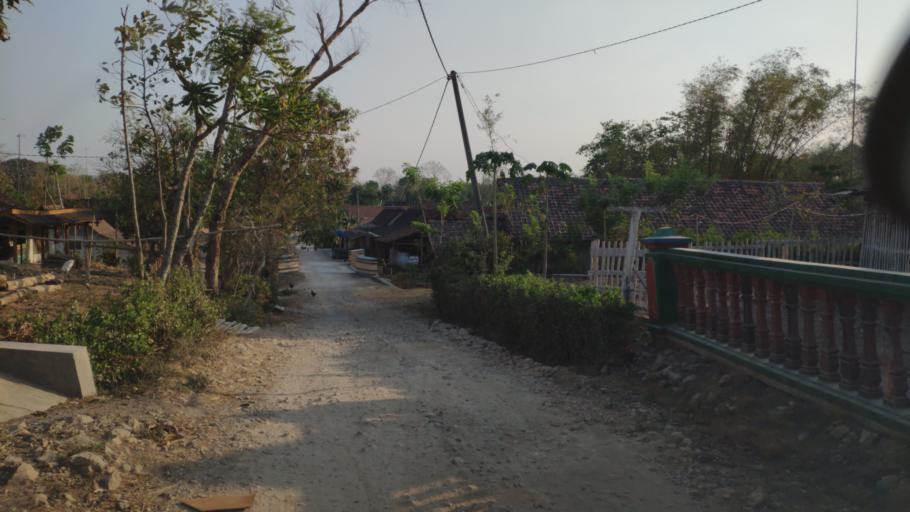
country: ID
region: Central Java
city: Jepang Satu
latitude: -7.0206
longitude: 111.4256
